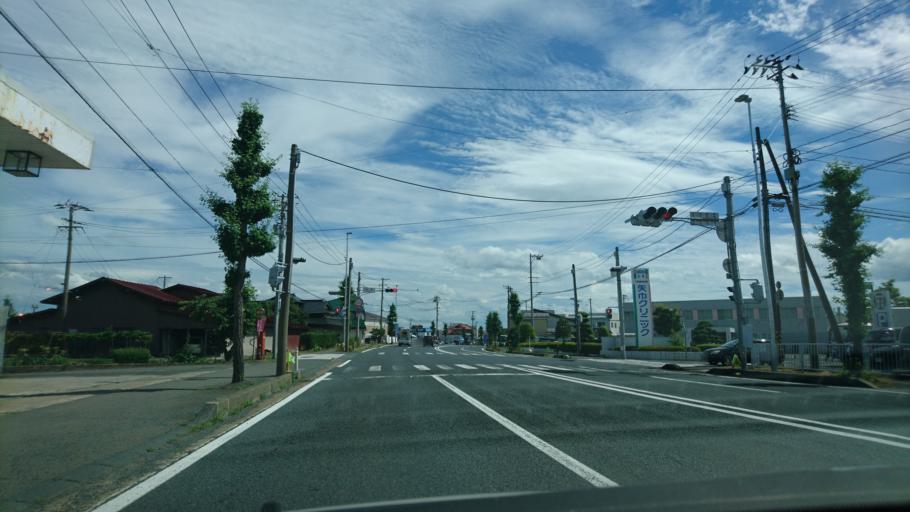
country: JP
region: Iwate
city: Morioka-shi
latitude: 39.6278
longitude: 141.1746
